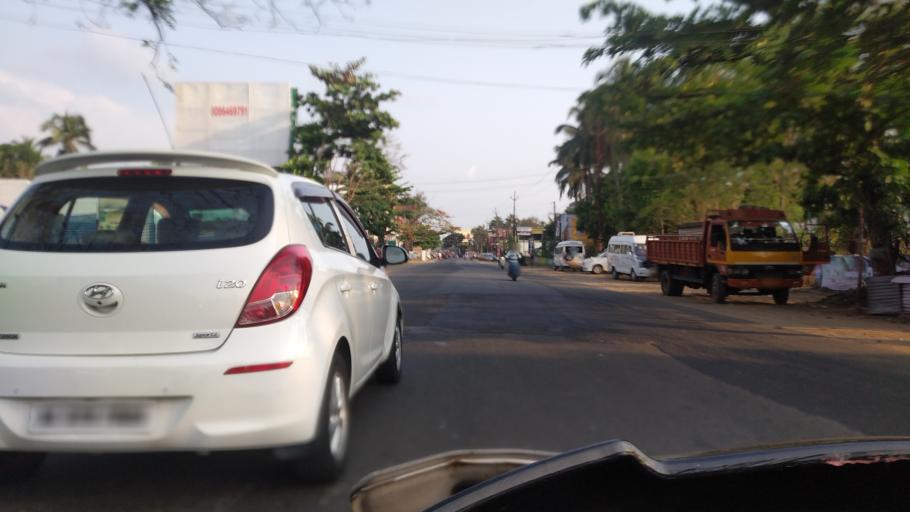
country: IN
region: Kerala
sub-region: Thrissur District
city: Thanniyam
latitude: 10.4179
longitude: 76.1058
